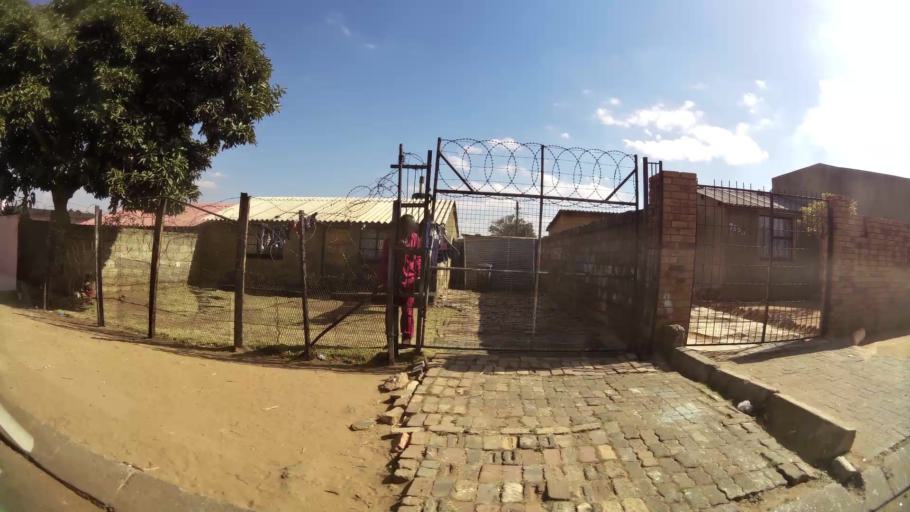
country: ZA
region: Gauteng
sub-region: City of Johannesburg Metropolitan Municipality
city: Soweto
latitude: -26.2323
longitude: 27.8971
